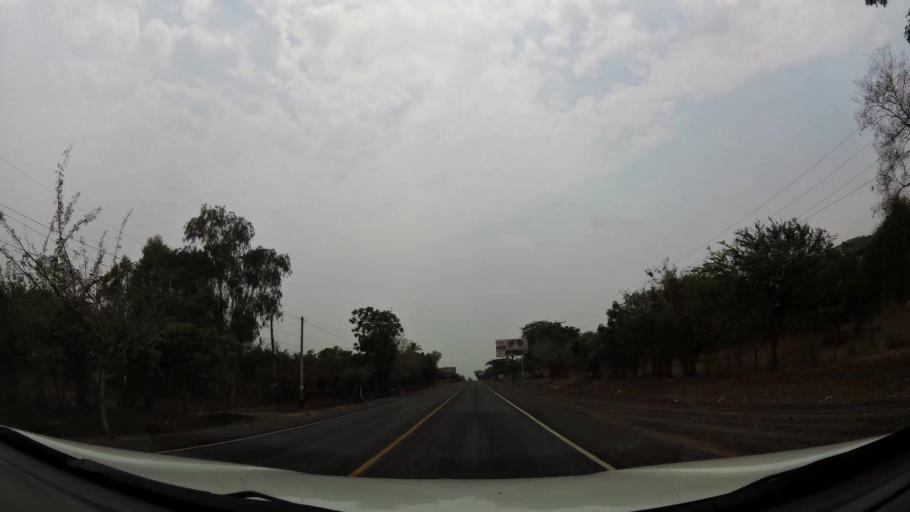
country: NI
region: Chinandega
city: Chichigalpa
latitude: 12.6044
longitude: -87.0542
